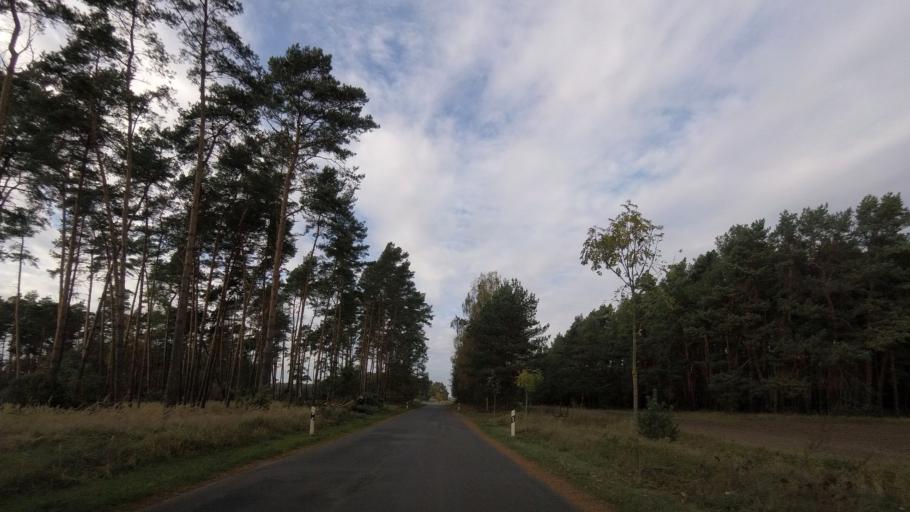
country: DE
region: Brandenburg
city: Beelitz
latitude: 52.1808
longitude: 12.9631
